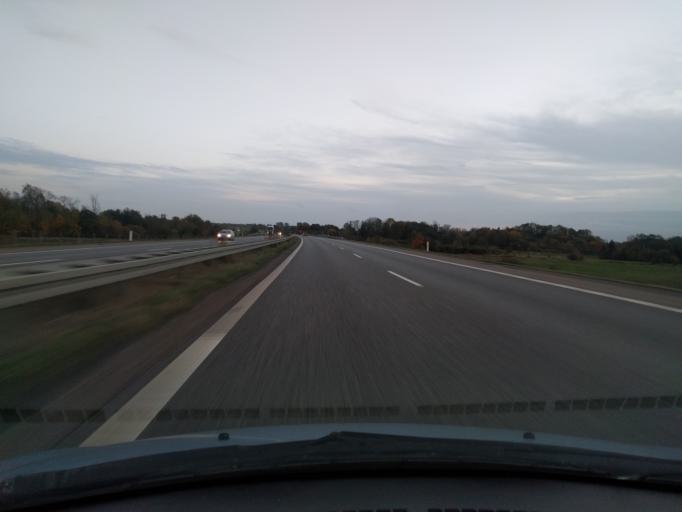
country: DK
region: South Denmark
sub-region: Faaborg-Midtfyn Kommune
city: Arslev
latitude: 55.2953
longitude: 10.4393
